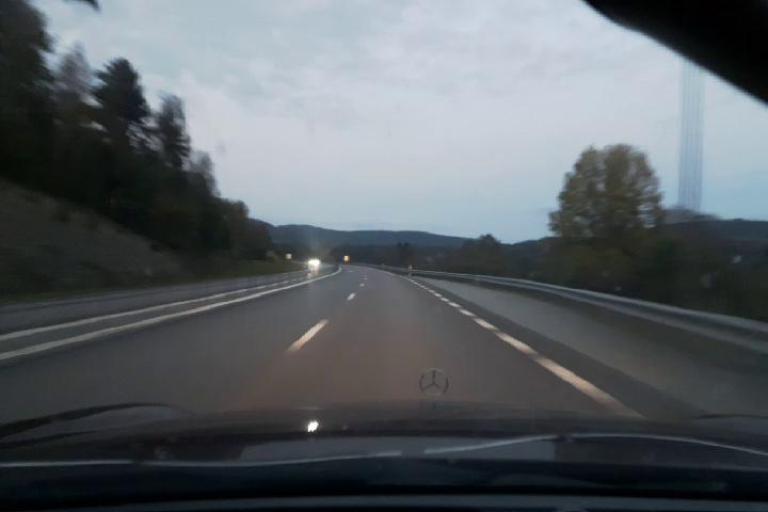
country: SE
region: Vaesternorrland
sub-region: Kramfors Kommun
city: Nordingra
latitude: 62.9640
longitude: 18.1518
